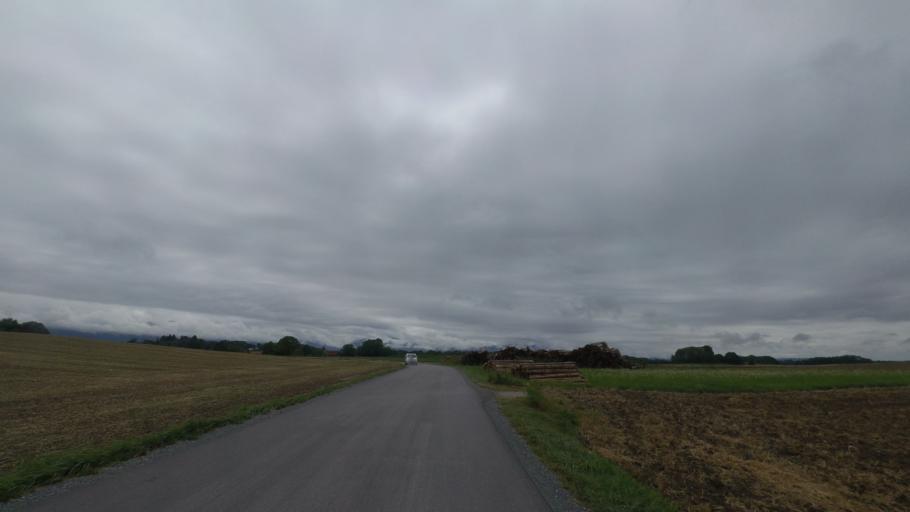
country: DE
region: Bavaria
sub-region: Upper Bavaria
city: Chieming
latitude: 47.9121
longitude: 12.5265
